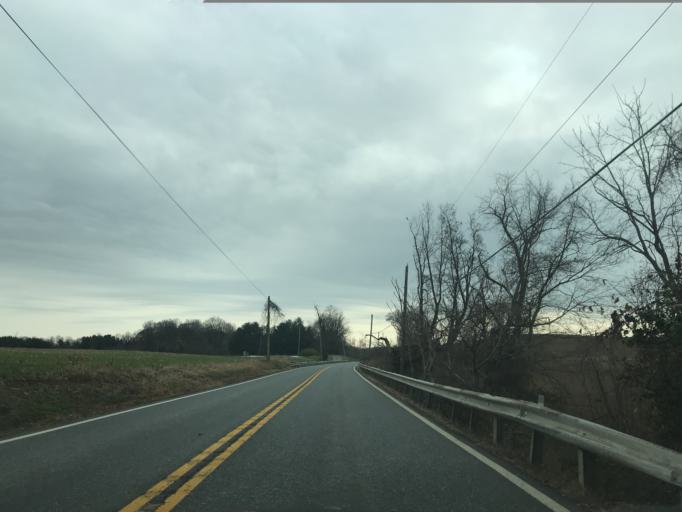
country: US
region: Maryland
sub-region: Harford County
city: Bel Air North
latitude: 39.6291
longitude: -76.3281
